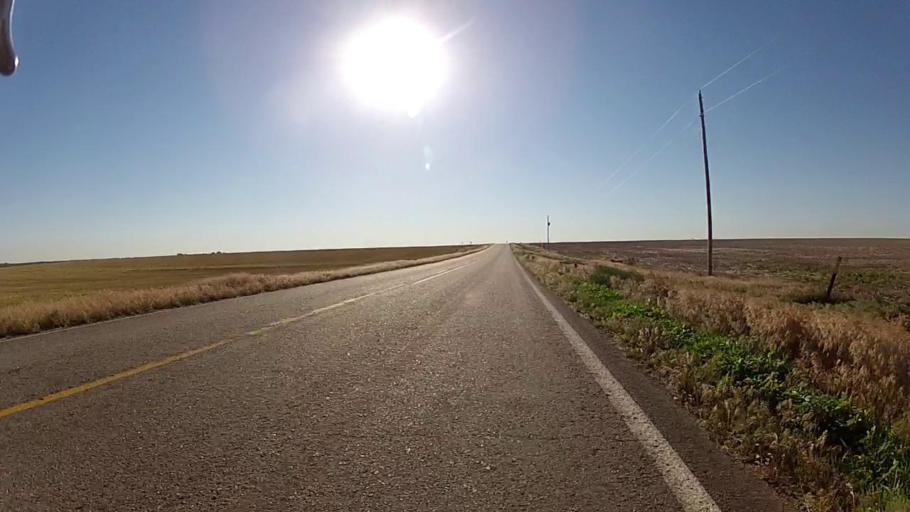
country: US
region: Kansas
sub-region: Ford County
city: Dodge City
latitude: 37.6462
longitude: -99.8330
